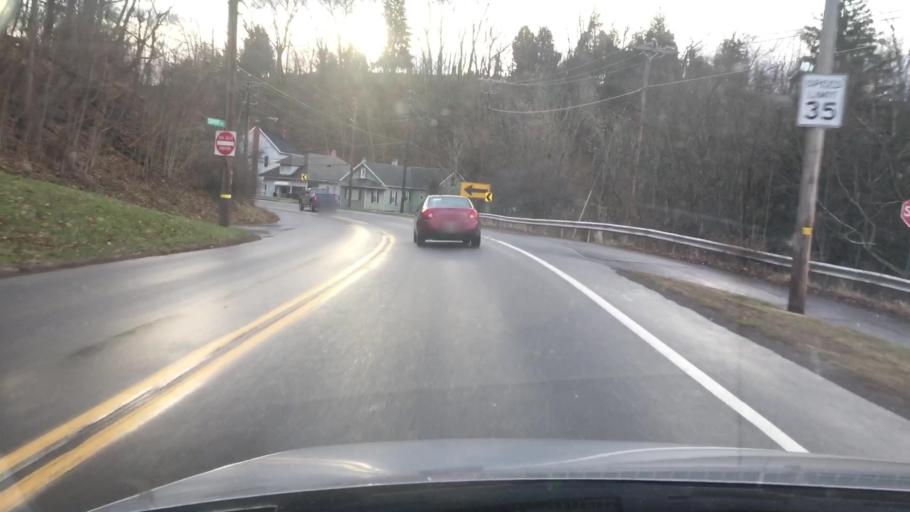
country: US
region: Pennsylvania
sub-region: Columbia County
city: Bloomsburg
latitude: 41.0068
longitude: -76.4607
